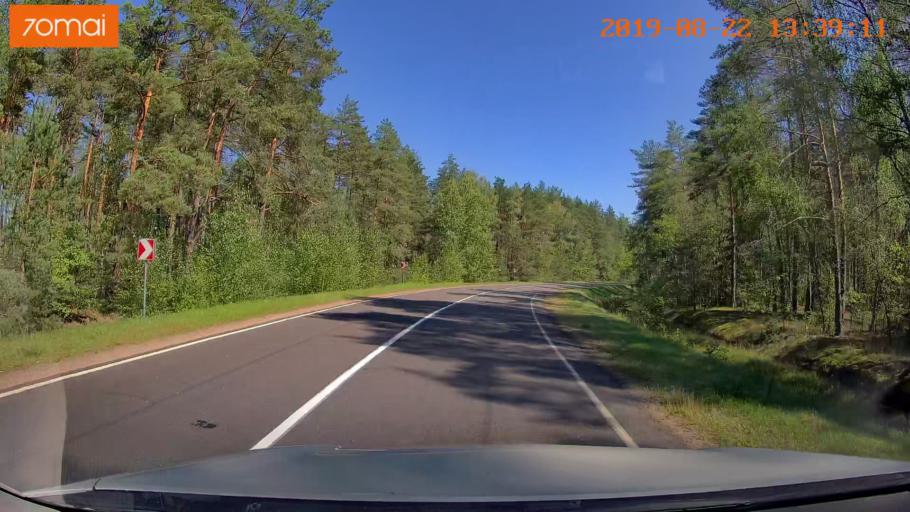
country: BY
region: Minsk
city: Staryya Darohi
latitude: 53.2279
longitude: 28.3433
